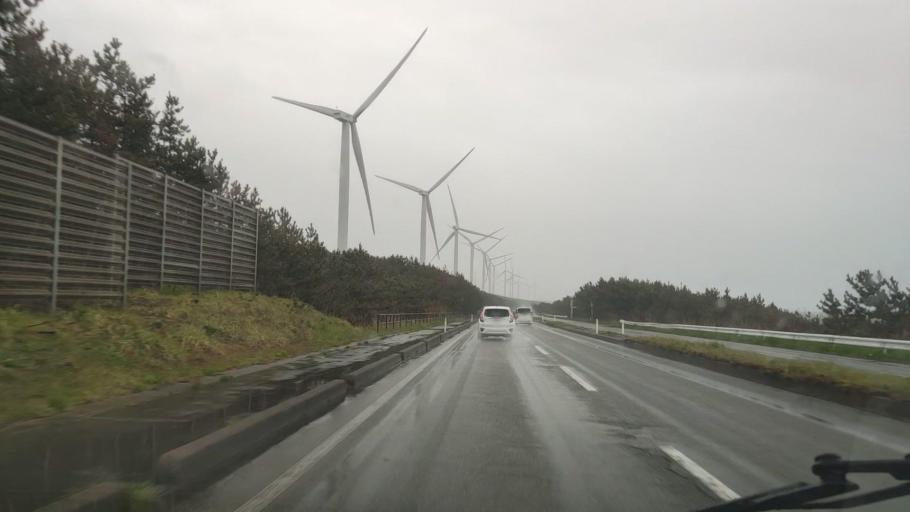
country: JP
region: Akita
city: Tenno
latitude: 39.8187
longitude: 140.0277
